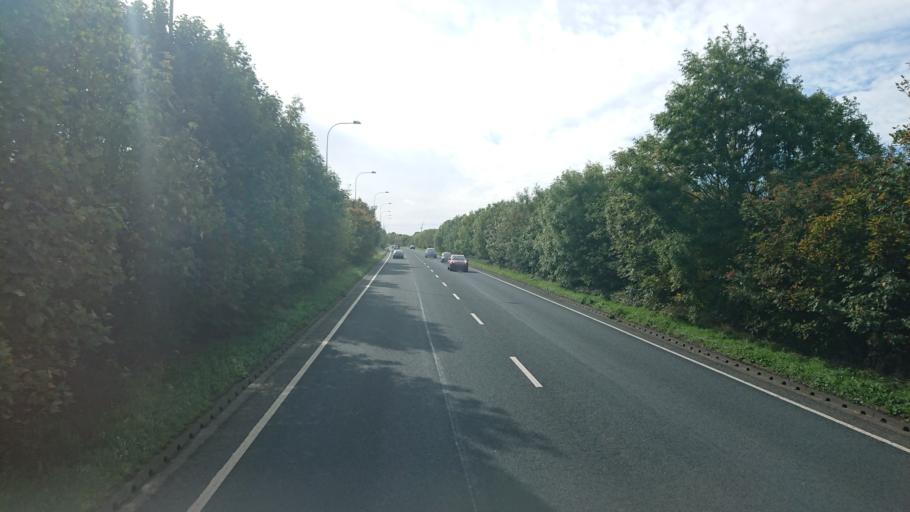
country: GB
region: England
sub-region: Lancashire
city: Morecambe
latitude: 54.0504
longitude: -2.8459
